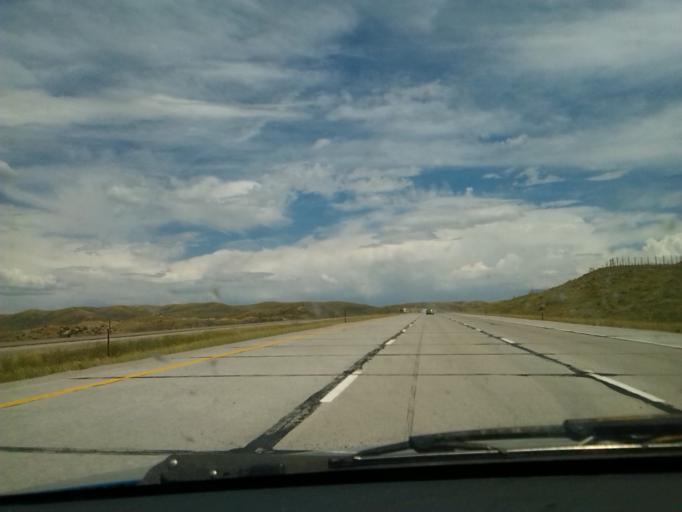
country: US
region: Wyoming
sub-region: Carbon County
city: Saratoga
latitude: 41.7310
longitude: -106.6724
